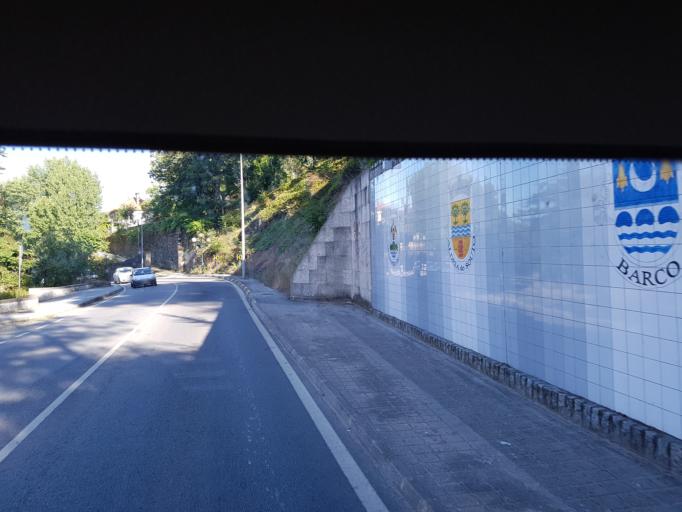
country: PT
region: Castelo Branco
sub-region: Covilha
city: Covilha
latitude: 40.2765
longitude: -7.5090
